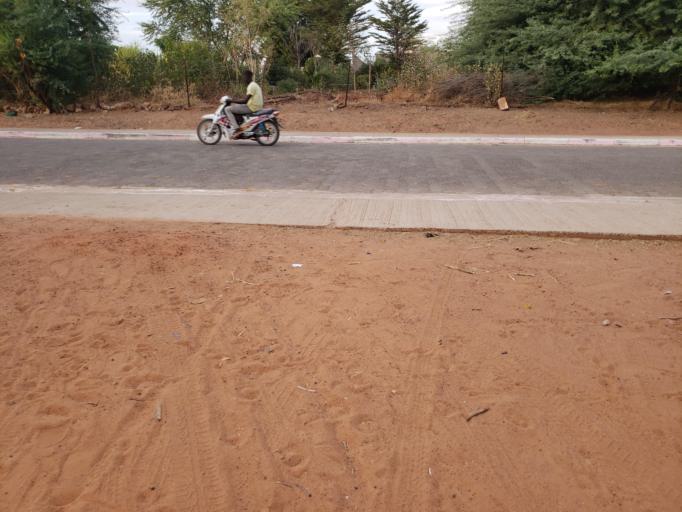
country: SN
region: Louga
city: Ndibene Dahra
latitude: 15.3990
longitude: -15.1117
